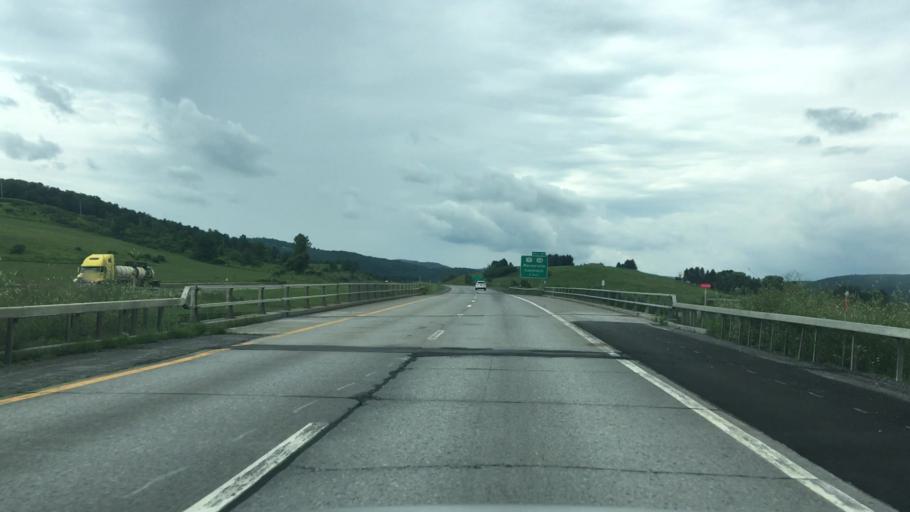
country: US
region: New York
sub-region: Schoharie County
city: Cobleskill
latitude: 42.6682
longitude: -74.4890
